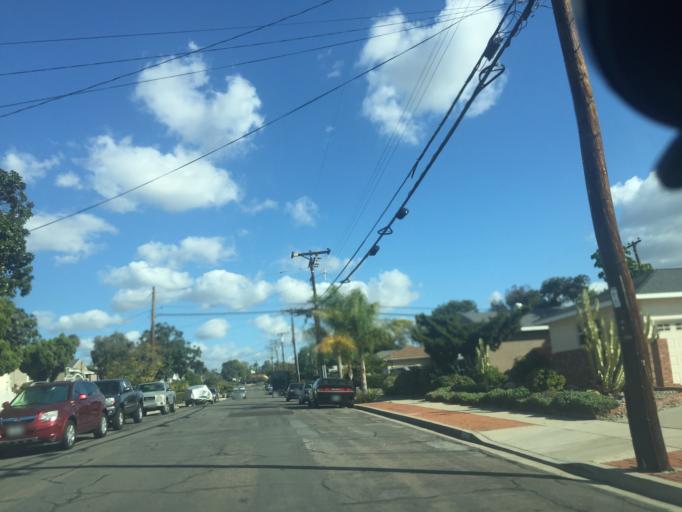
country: US
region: California
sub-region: San Diego County
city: La Mesa
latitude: 32.7842
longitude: -117.0882
